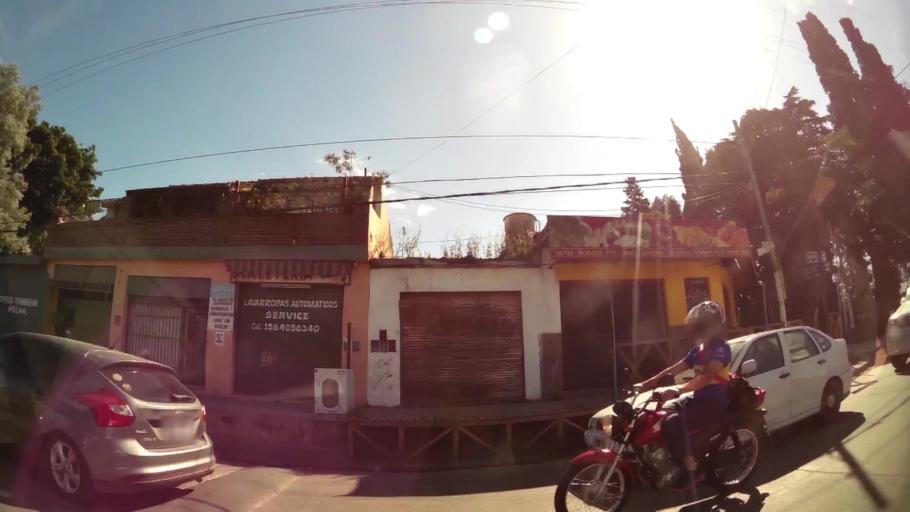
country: AR
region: Buenos Aires
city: Santa Catalina - Dique Lujan
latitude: -34.4798
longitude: -58.7009
